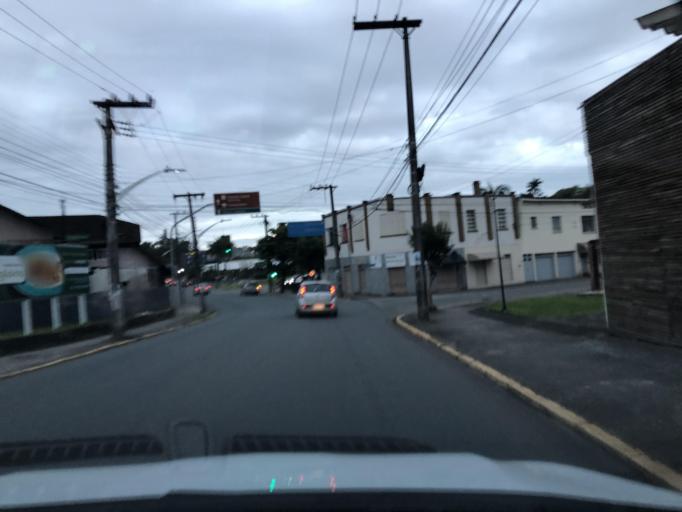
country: BR
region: Santa Catarina
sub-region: Joinville
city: Joinville
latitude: -26.2962
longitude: -48.8656
